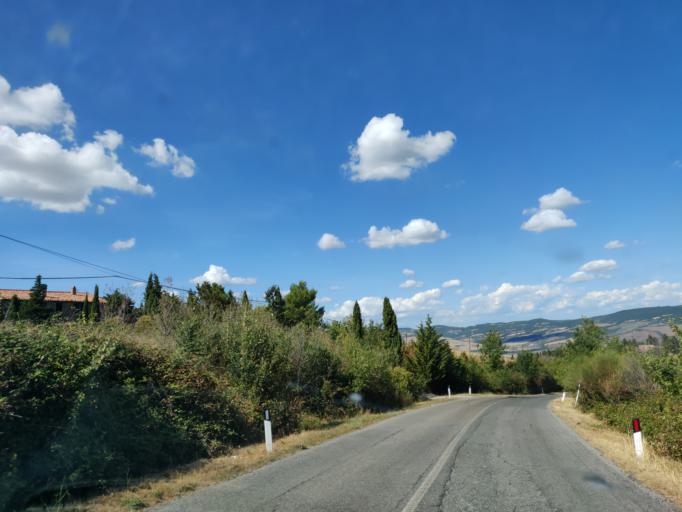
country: IT
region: Tuscany
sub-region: Provincia di Siena
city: Radicofani
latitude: 42.9678
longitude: 11.7335
